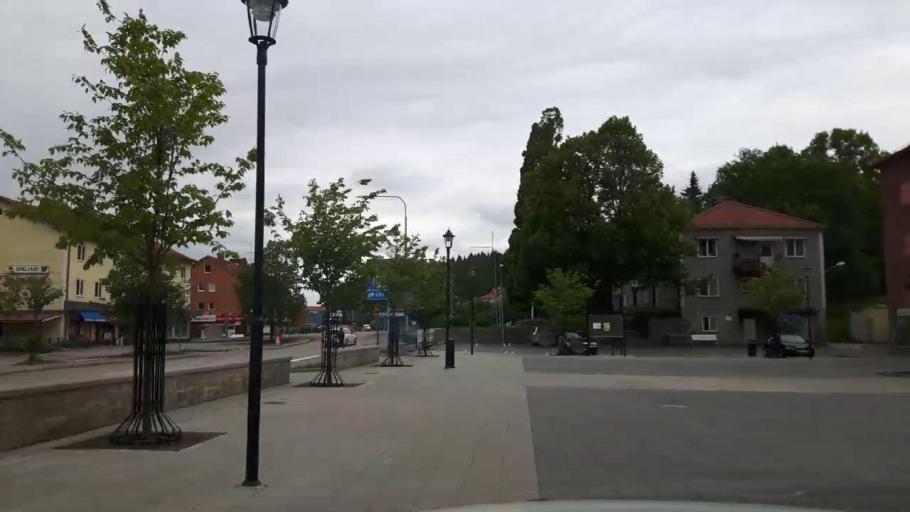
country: SE
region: Vaestmanland
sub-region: Kopings Kommun
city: Kolsva
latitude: 59.5999
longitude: 15.8431
